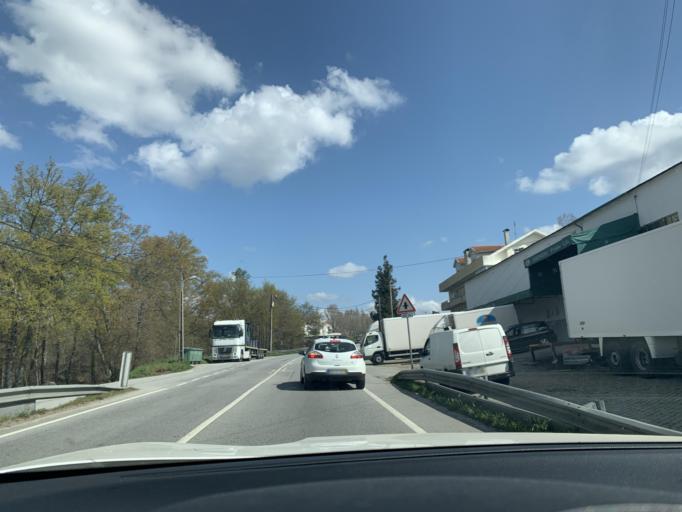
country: PT
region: Viseu
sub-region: Viseu
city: Rio de Loba
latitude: 40.6839
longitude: -7.8817
